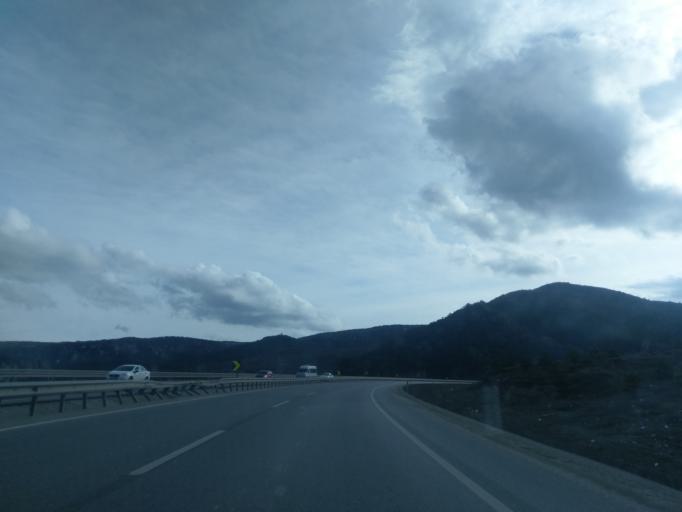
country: TR
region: Kuetahya
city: Sabuncu
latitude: 39.5615
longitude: 30.0763
